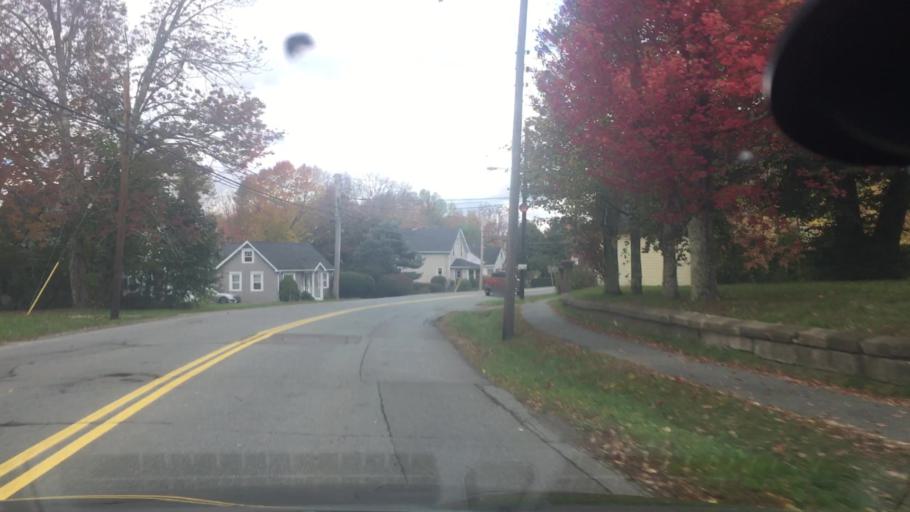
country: CA
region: Nova Scotia
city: Windsor
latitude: 44.9788
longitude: -64.1276
